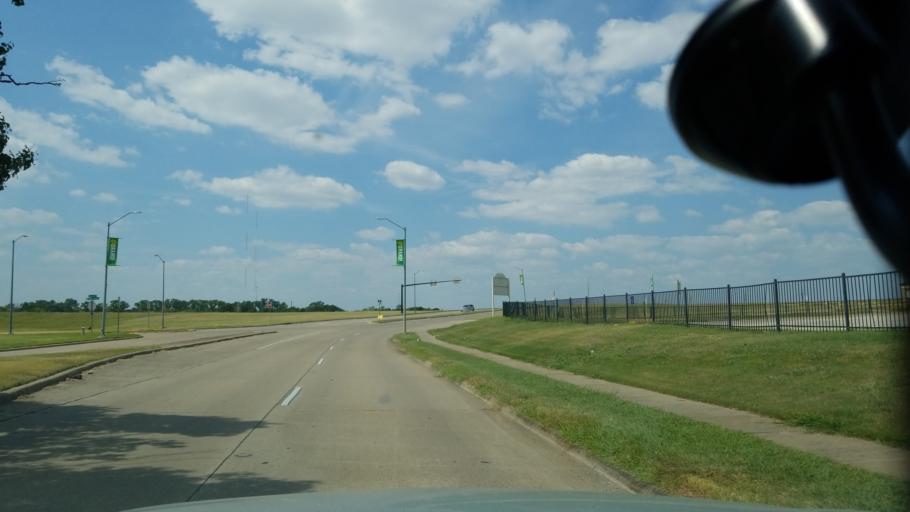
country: US
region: Texas
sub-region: Dallas County
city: Grand Prairie
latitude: 32.7684
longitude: -96.9883
